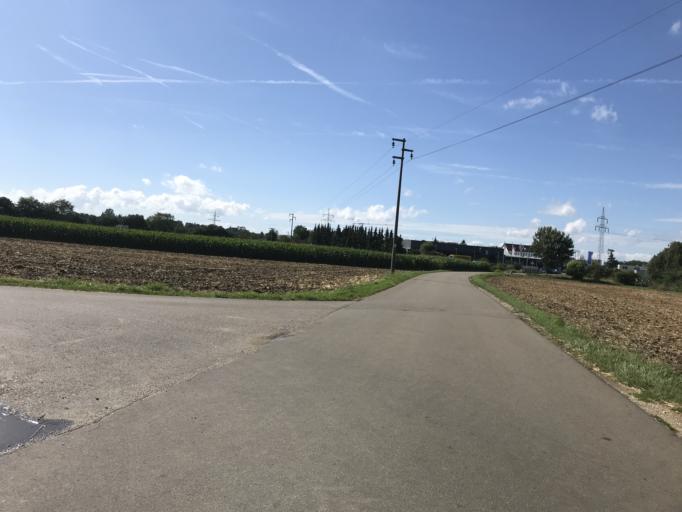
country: DE
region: Baden-Wuerttemberg
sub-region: Tuebingen Region
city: Langenau
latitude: 48.4847
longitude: 10.1251
